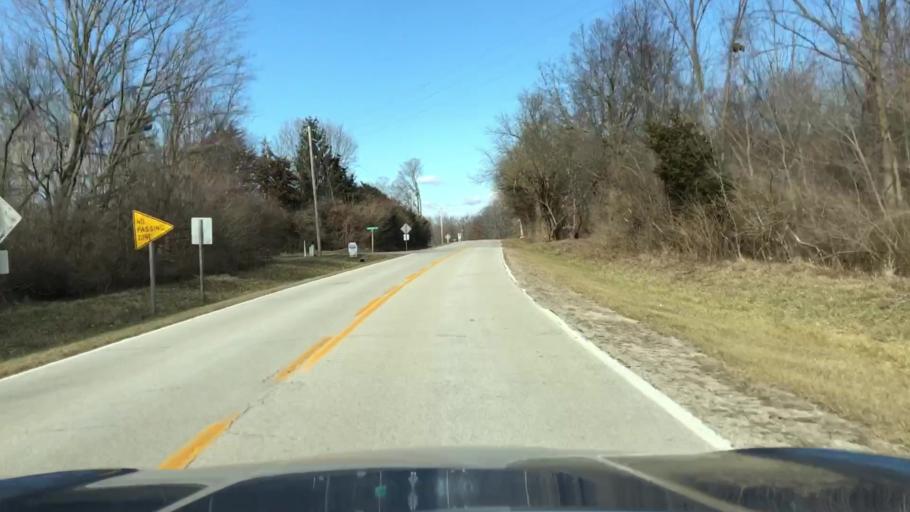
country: US
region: Illinois
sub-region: McLean County
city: Hudson
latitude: 40.6556
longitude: -88.9242
